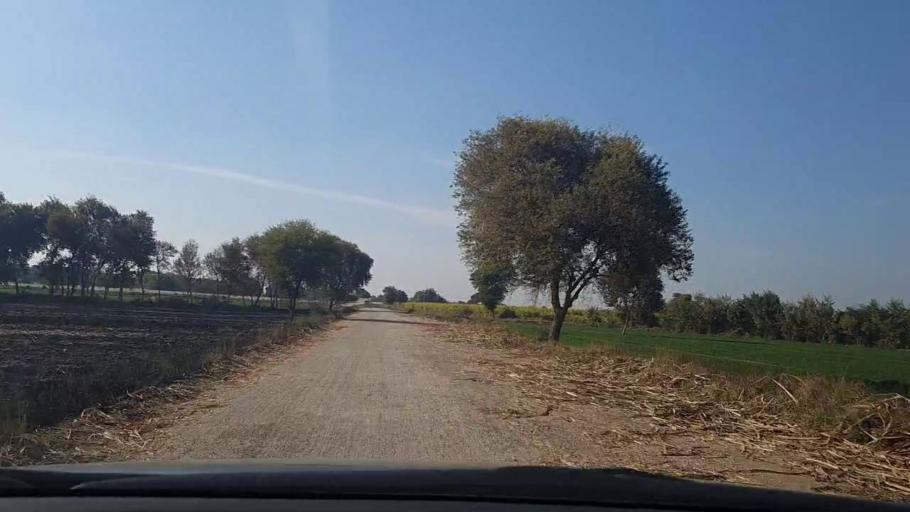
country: PK
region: Sindh
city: Sehwan
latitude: 26.3358
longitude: 67.9801
